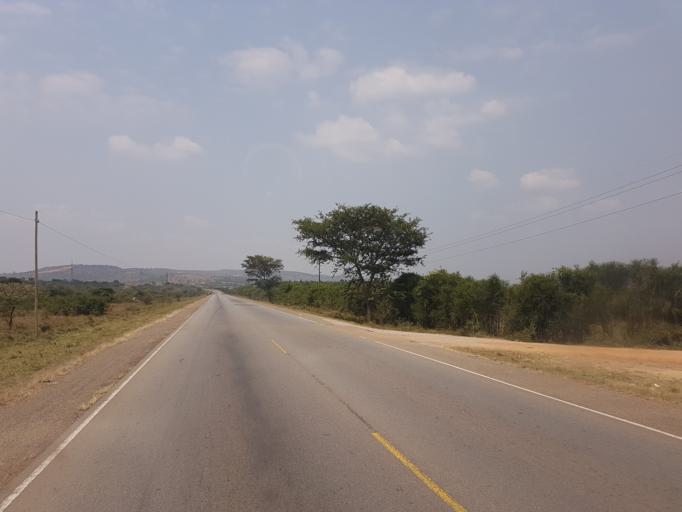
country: UG
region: Western Region
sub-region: Mbarara District
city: Mbarara
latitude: -0.5099
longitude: 30.8312
